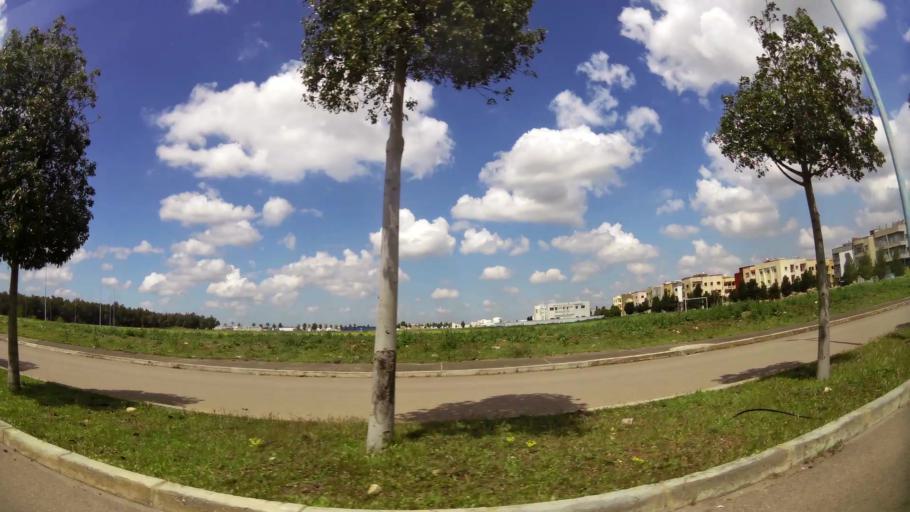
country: MA
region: Grand Casablanca
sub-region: Mediouna
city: Mediouna
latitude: 33.3876
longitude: -7.5485
